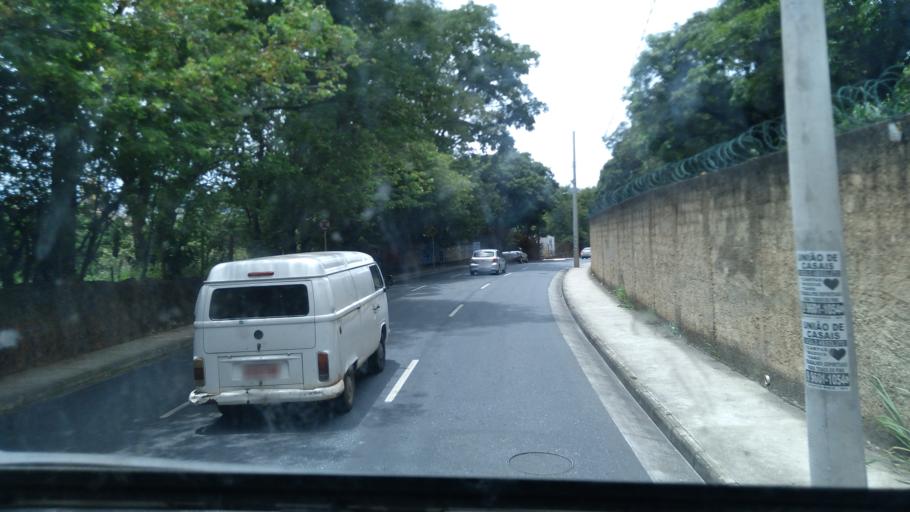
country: BR
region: Minas Gerais
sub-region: Belo Horizonte
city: Belo Horizonte
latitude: -19.8880
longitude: -43.9127
